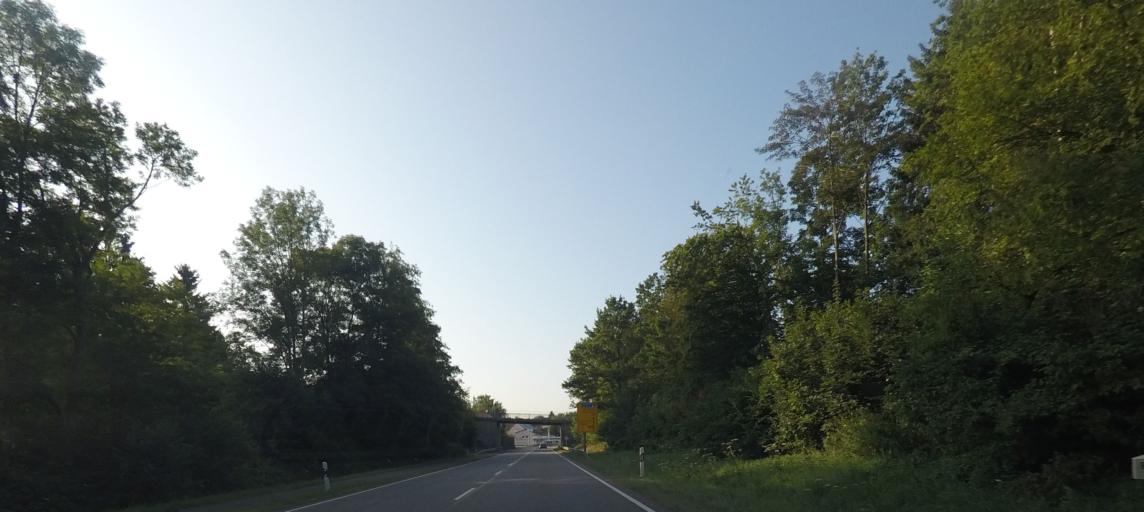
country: DE
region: Saarland
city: Heusweiler
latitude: 49.3604
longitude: 6.9286
